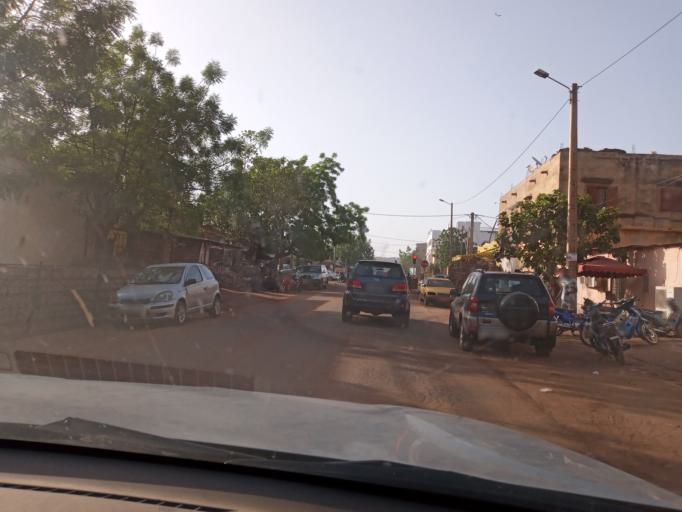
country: ML
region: Bamako
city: Bamako
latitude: 12.6625
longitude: -7.9728
